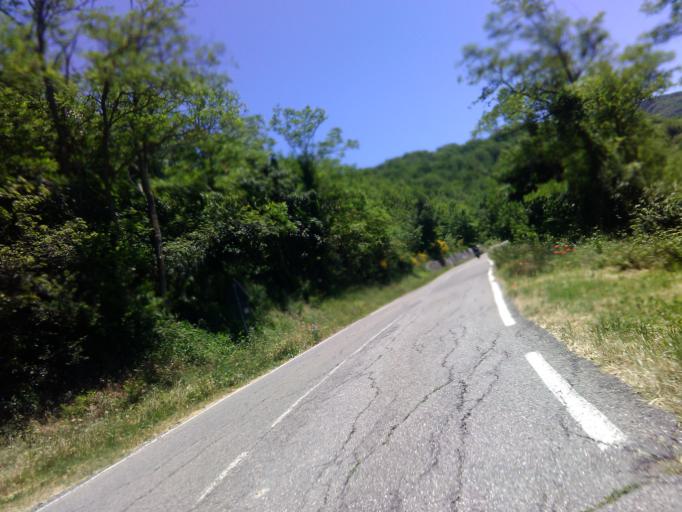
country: IT
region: Emilia-Romagna
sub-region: Provincia di Parma
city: Calestano
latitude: 44.5916
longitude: 10.1457
